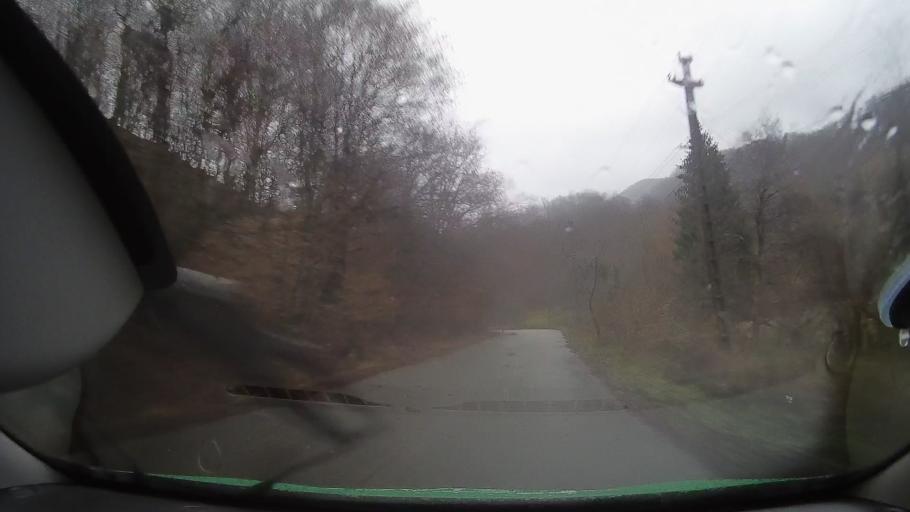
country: RO
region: Alba
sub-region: Comuna Avram Iancu
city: Avram Iancu
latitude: 46.2980
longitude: 22.7580
